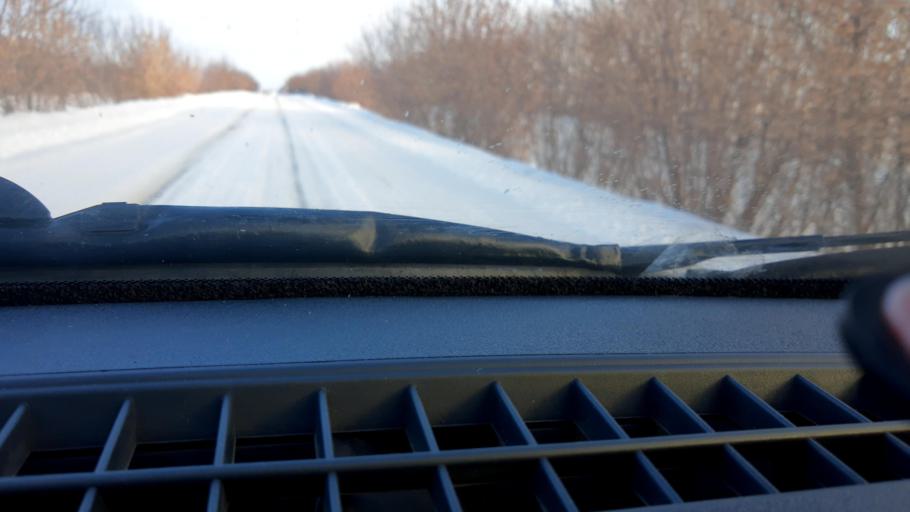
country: RU
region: Bashkortostan
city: Kushnarenkovo
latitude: 55.1146
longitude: 55.5585
